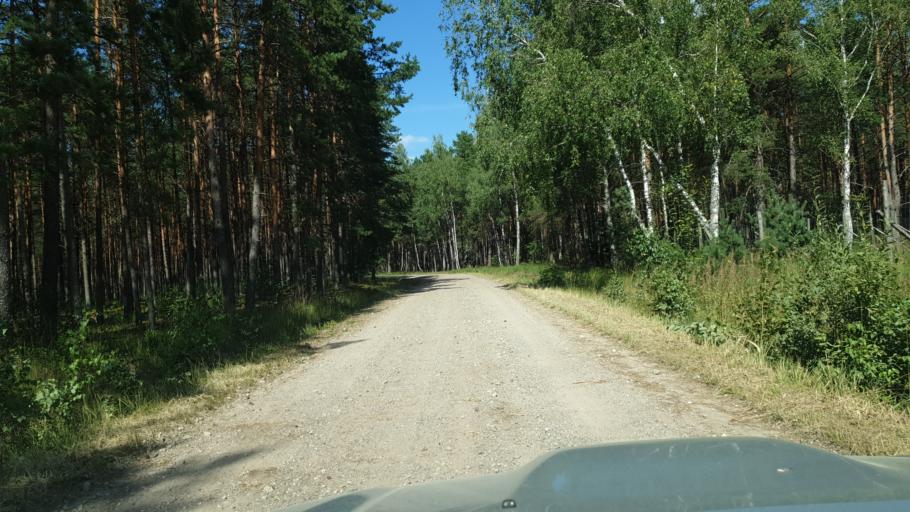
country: LT
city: Sirvintos
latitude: 54.9034
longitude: 24.9562
